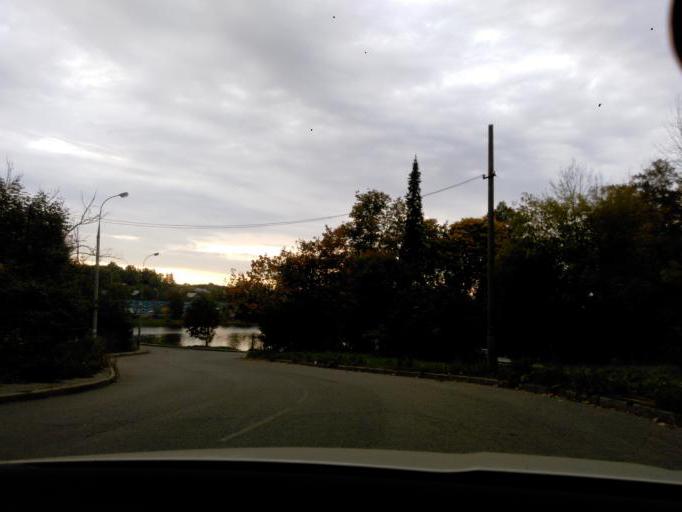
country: RU
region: Moscow
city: Severnyy
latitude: 55.9426
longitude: 37.5398
